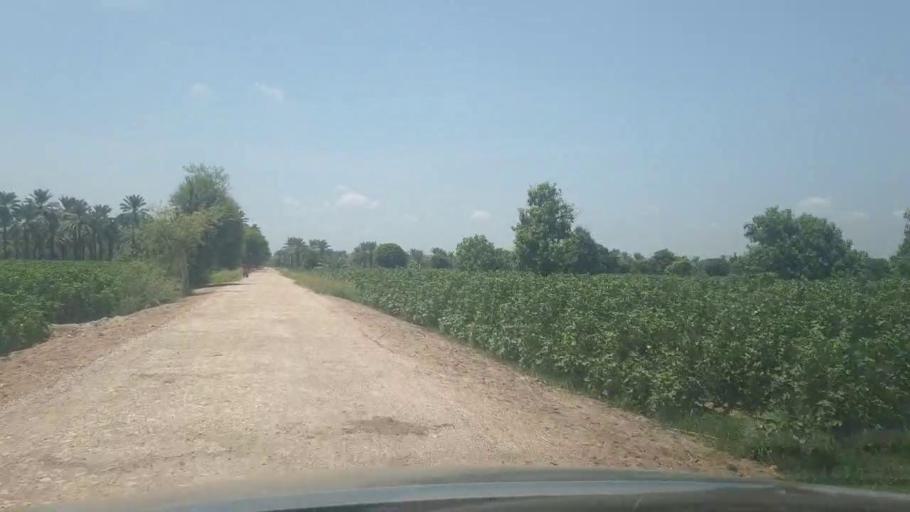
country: PK
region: Sindh
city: Kot Diji
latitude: 27.3888
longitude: 68.6901
